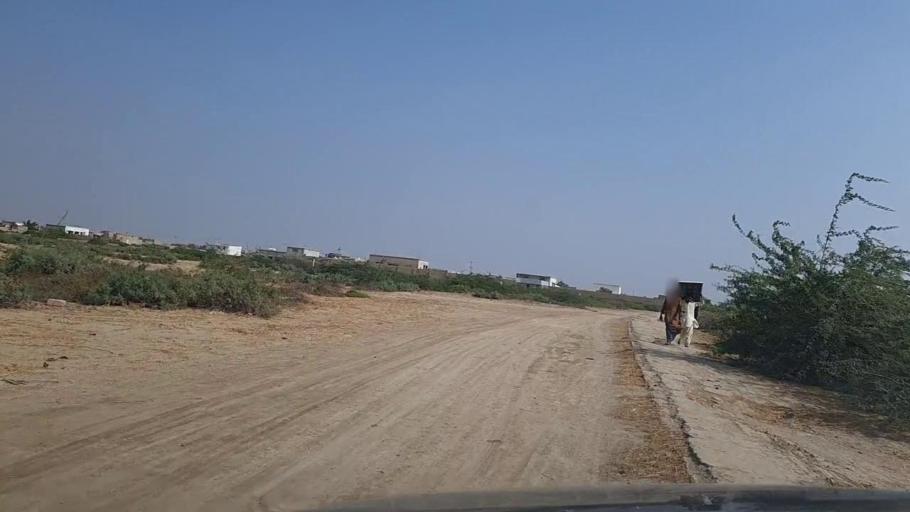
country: PK
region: Sindh
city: Gharo
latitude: 24.7412
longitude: 67.6710
